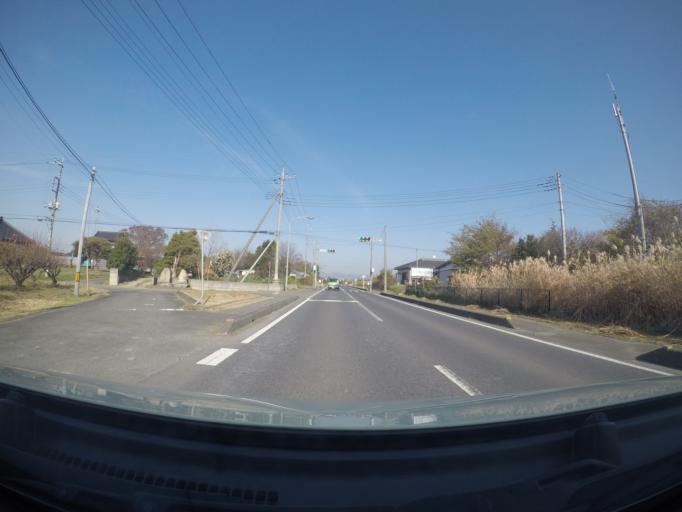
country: JP
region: Ibaraki
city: Makabe
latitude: 36.2513
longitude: 140.0726
